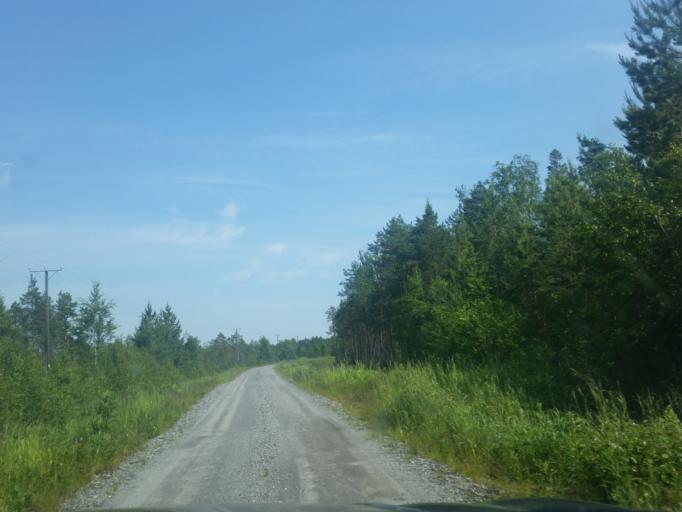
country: FI
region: Northern Savo
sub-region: Ylae-Savo
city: Keitele
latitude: 63.1010
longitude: 26.5492
